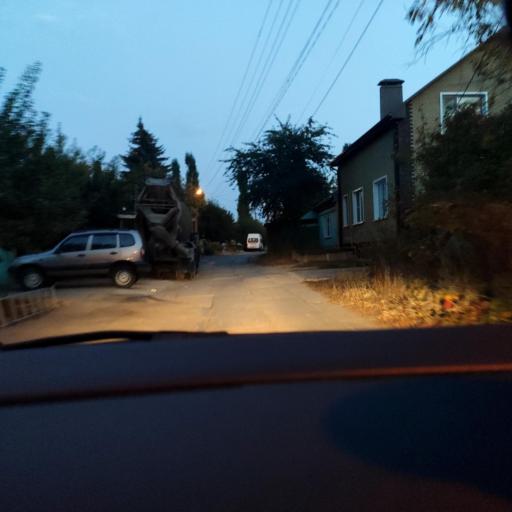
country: RU
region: Voronezj
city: Voronezh
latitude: 51.6812
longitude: 39.1606
